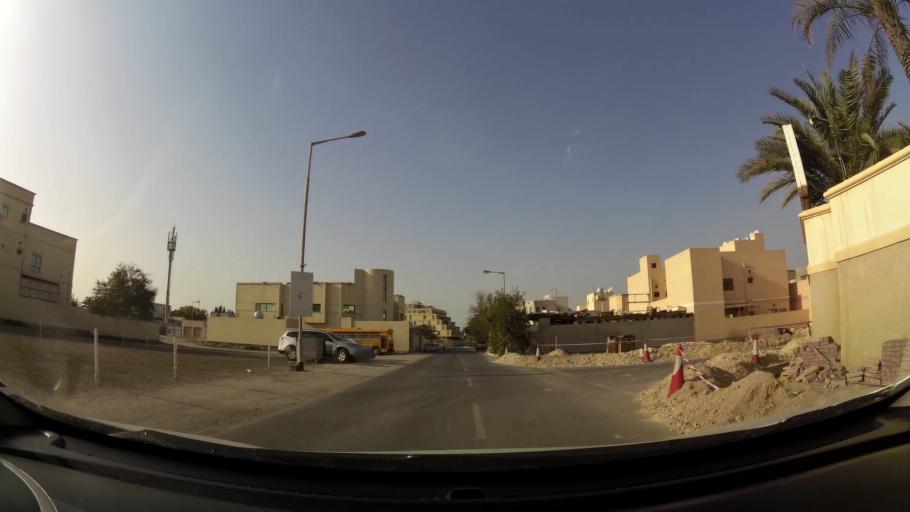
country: BH
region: Manama
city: Jidd Hafs
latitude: 26.2159
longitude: 50.4966
